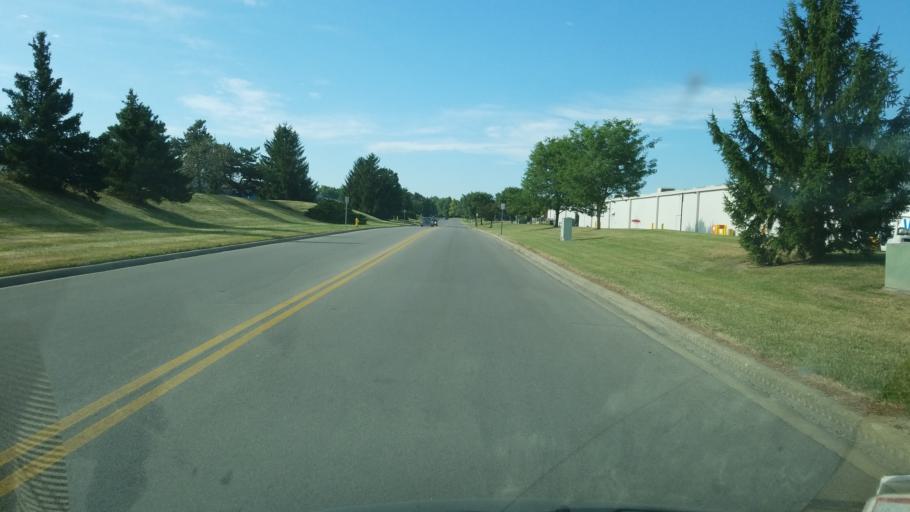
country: US
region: Ohio
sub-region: Delaware County
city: Lewis Center
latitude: 40.1662
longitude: -83.0151
